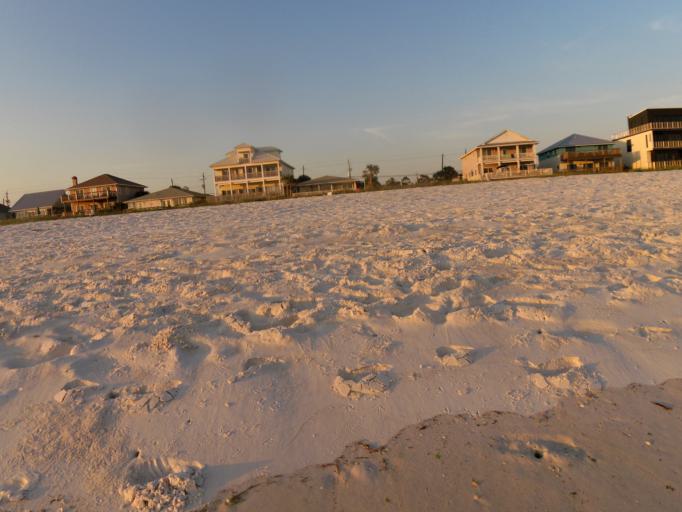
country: US
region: Florida
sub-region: Bay County
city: Laguna Beach
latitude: 30.2171
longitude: -85.8818
